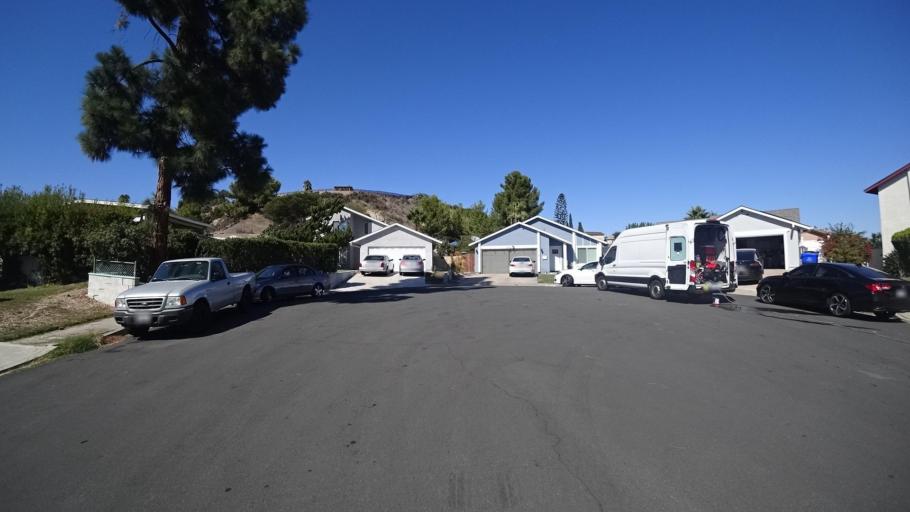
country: US
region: California
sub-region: San Diego County
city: La Presa
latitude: 32.7007
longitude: -117.0239
